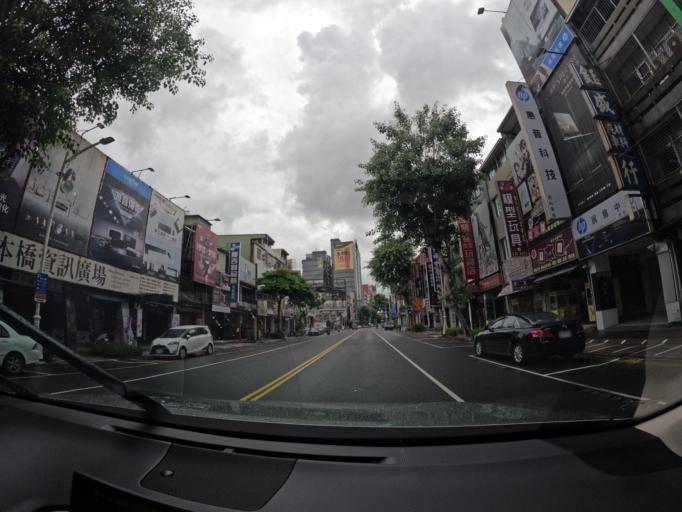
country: TW
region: Kaohsiung
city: Kaohsiung
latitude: 22.6375
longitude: 120.3099
